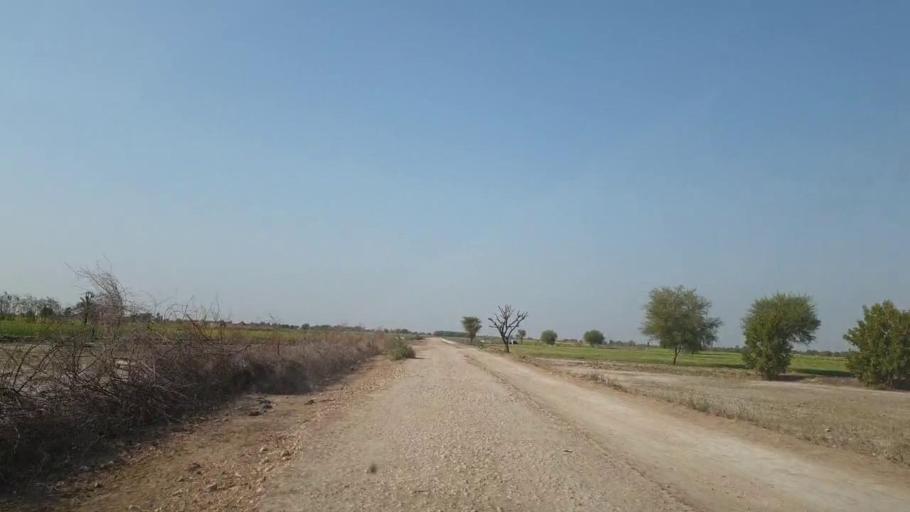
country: PK
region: Sindh
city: Tando Mittha Khan
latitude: 25.7555
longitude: 69.1963
